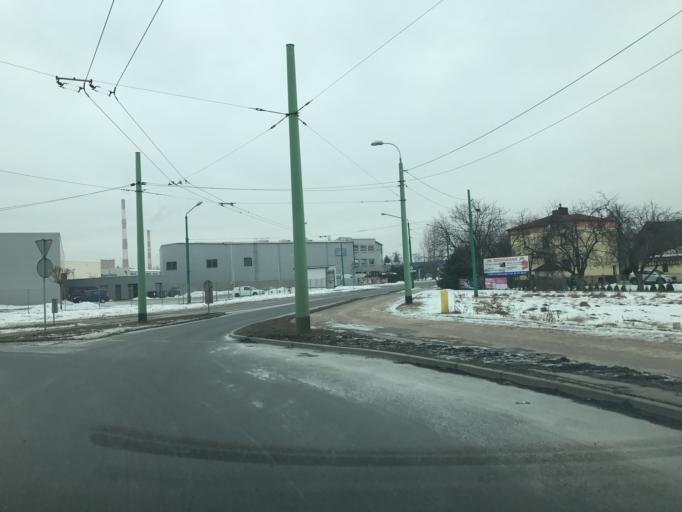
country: PL
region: Silesian Voivodeship
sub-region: Tychy
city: Cielmice
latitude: 50.1038
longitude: 19.0338
